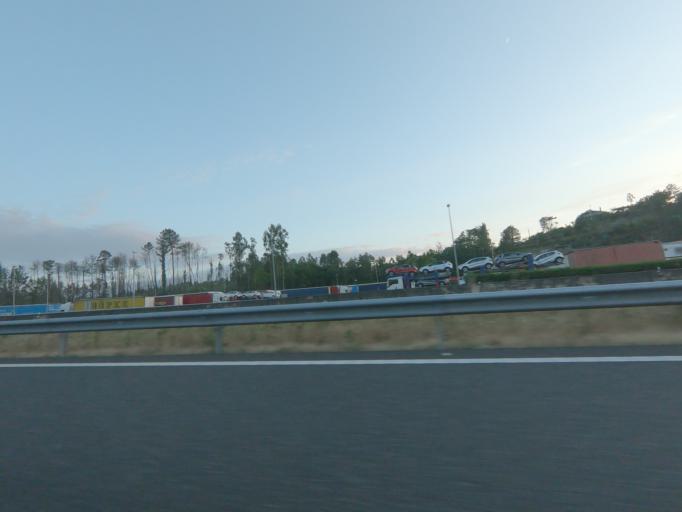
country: ES
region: Galicia
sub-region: Provincia de Pontevedra
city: Ponteareas
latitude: 42.1456
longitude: -8.4753
